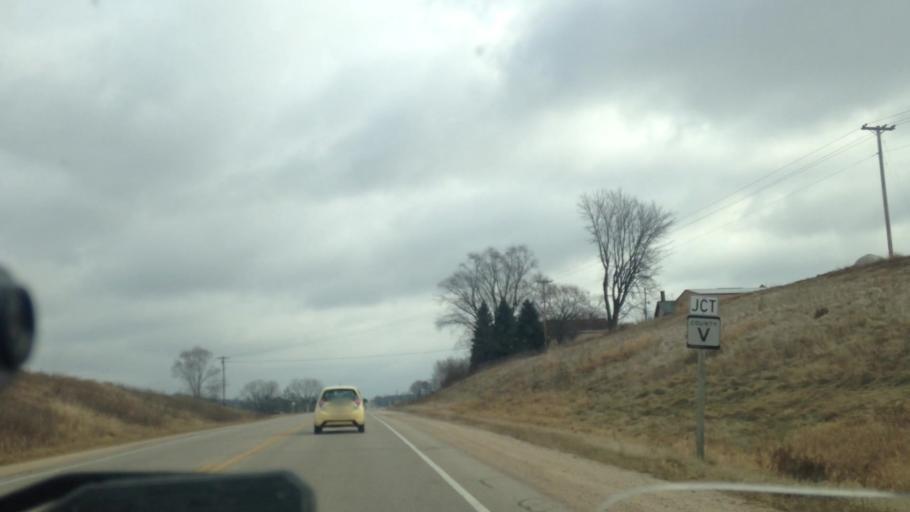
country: US
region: Wisconsin
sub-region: Dodge County
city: Mayville
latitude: 43.4431
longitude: -88.5651
